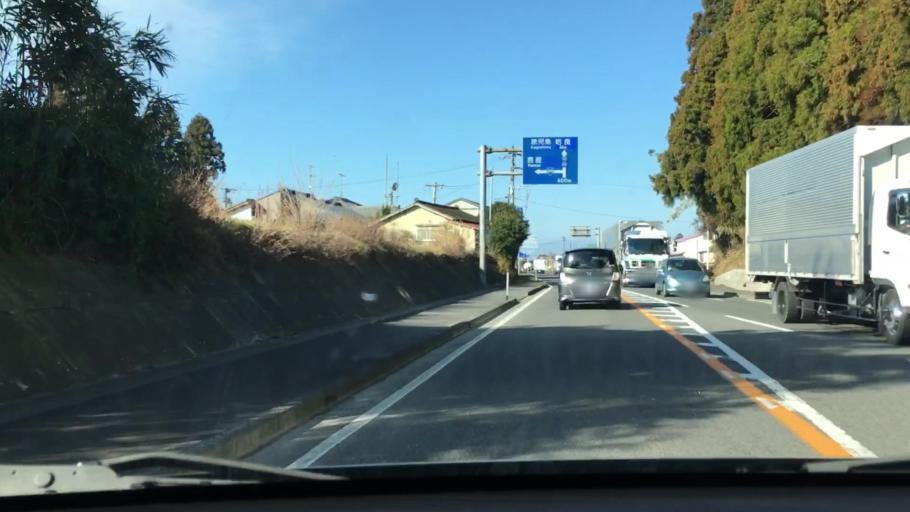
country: JP
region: Kagoshima
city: Kokubu-matsuki
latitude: 31.6723
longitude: 130.8499
